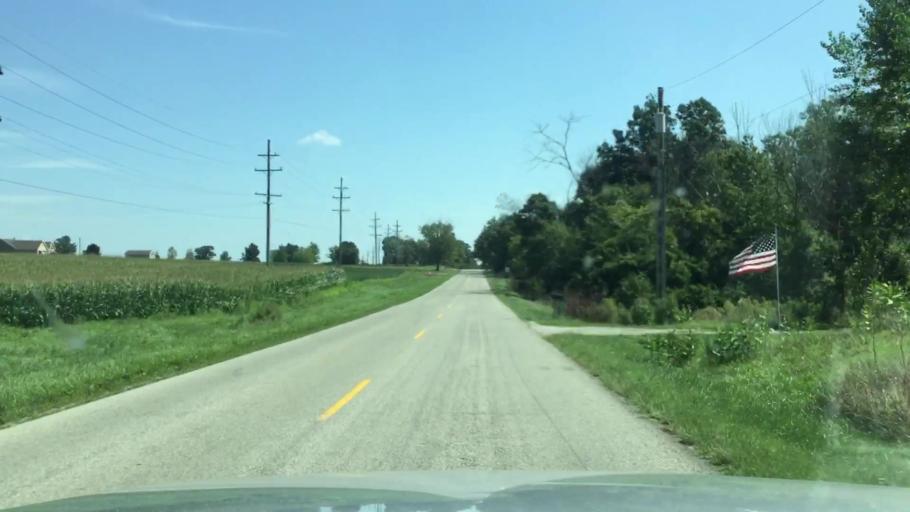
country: US
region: Michigan
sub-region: Lenawee County
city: Clinton
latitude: 42.0654
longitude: -83.9387
